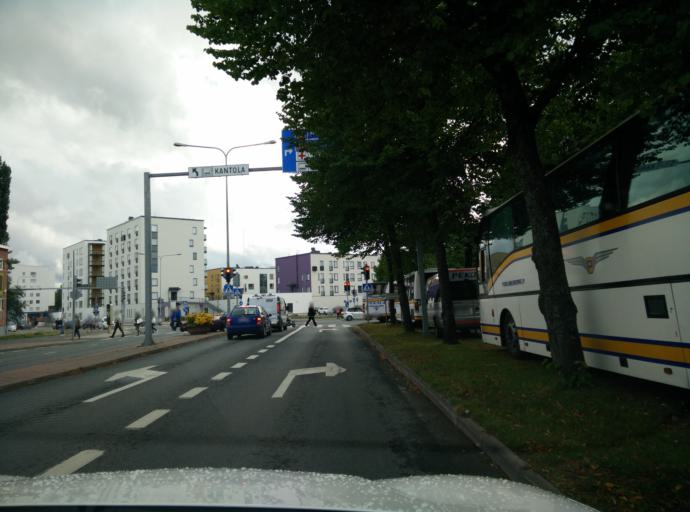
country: FI
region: Haeme
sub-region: Haemeenlinna
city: Haemeenlinna
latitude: 60.9975
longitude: 24.4787
